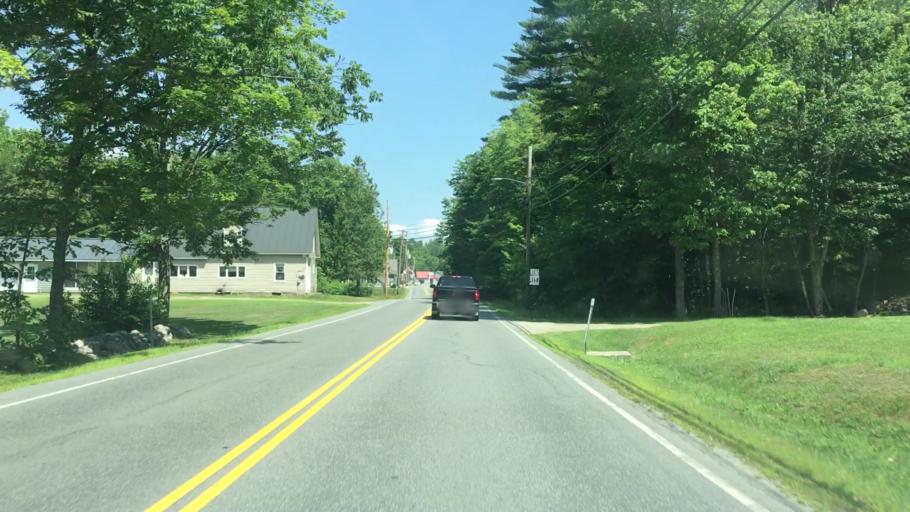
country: US
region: New Hampshire
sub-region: Sullivan County
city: Grantham
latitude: 43.4859
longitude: -72.1368
